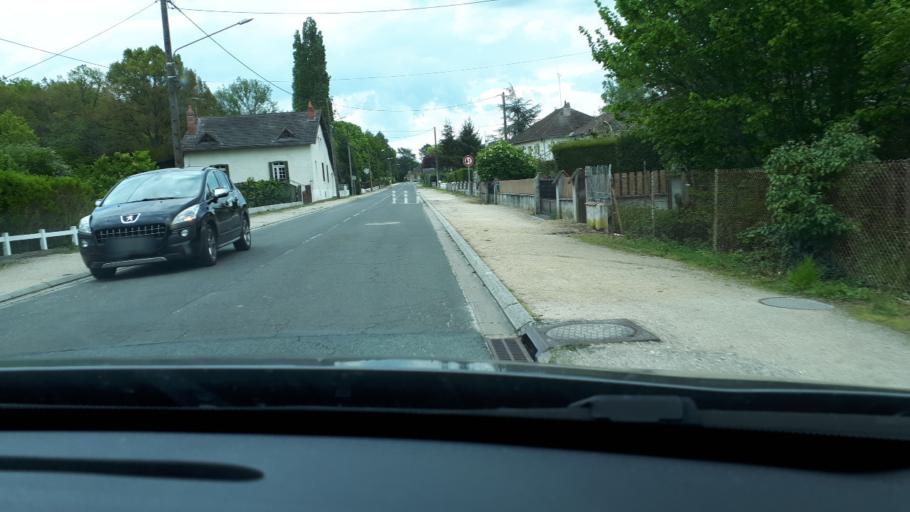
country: FR
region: Centre
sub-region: Departement du Loir-et-Cher
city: Nouan-le-Fuzelier
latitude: 47.5359
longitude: 2.0402
